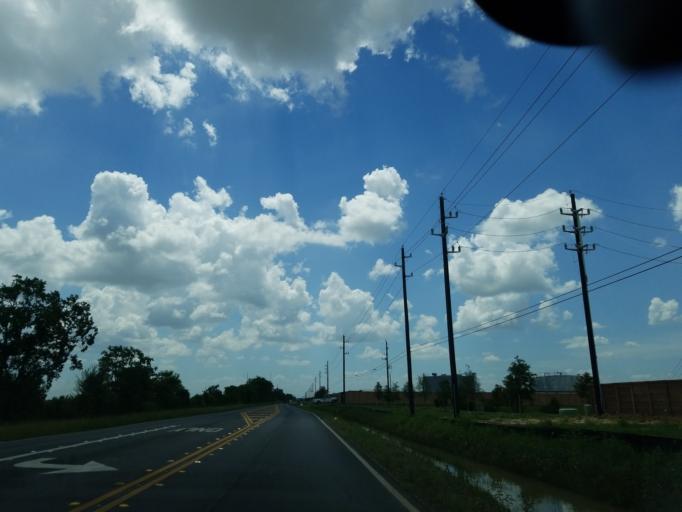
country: US
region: Texas
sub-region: Harris County
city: Katy
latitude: 29.8460
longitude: -95.7937
